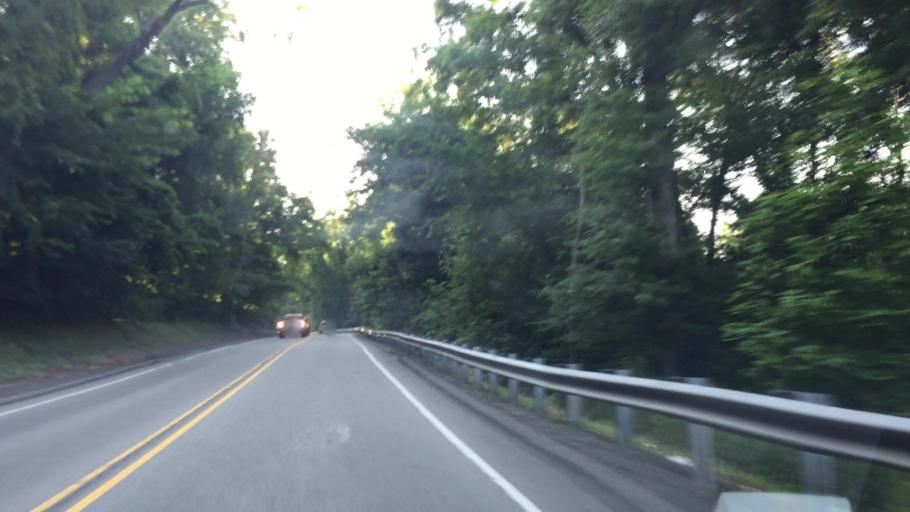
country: US
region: Pennsylvania
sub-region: Allegheny County
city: South Park Township
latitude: 40.3098
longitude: -79.9962
